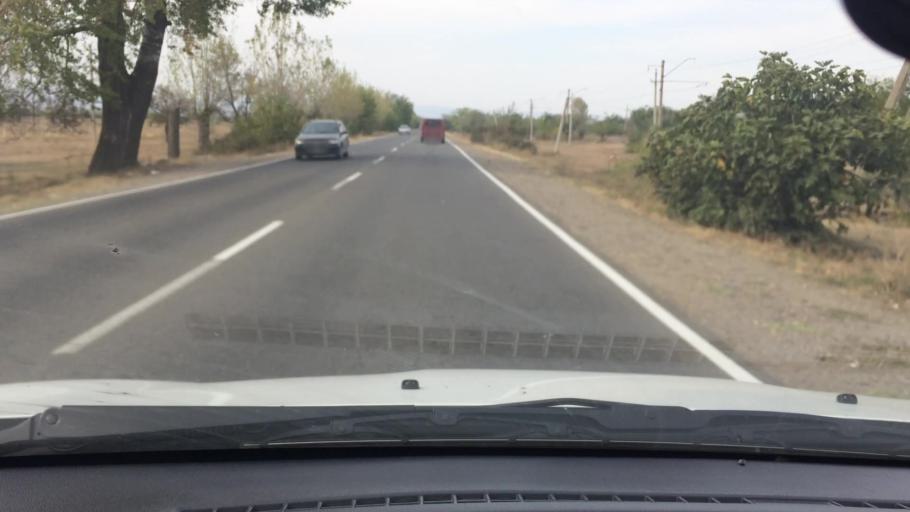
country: GE
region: Kvemo Kartli
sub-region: Marneuli
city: Marneuli
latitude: 41.4424
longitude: 44.8168
